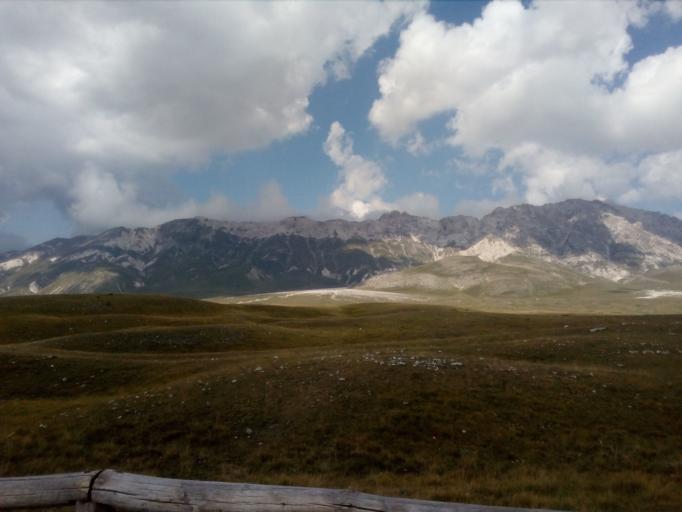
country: IT
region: Abruzzo
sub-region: Provincia dell' Aquila
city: Santo Stefano di Sessanio
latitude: 42.4026
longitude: 13.6402
